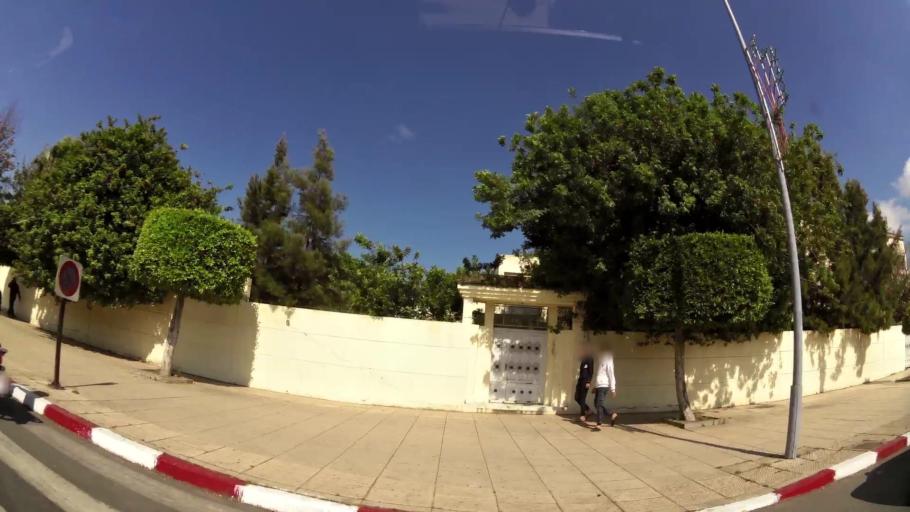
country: MA
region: Rabat-Sale-Zemmour-Zaer
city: Sale
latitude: 34.0394
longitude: -6.7854
